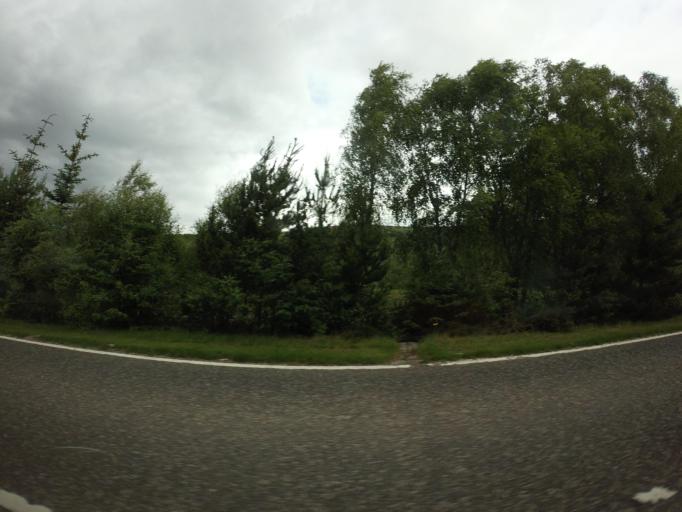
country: GB
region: Scotland
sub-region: Highland
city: Conon Bridge
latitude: 57.6601
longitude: -4.6760
